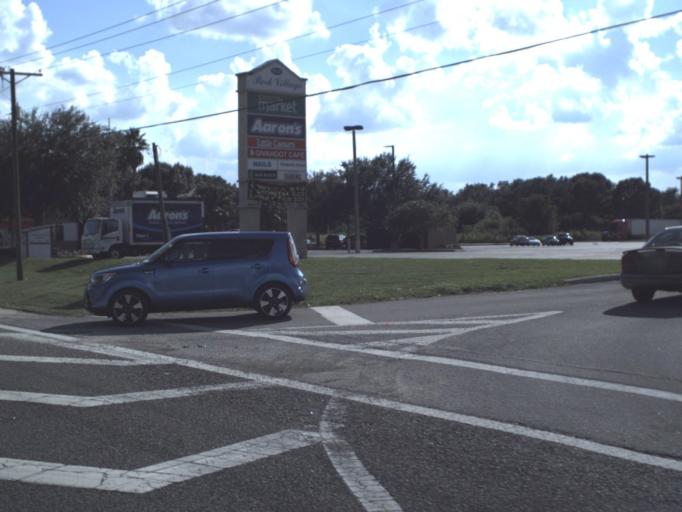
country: US
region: Florida
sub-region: Polk County
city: Medulla
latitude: 27.9378
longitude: -81.9742
